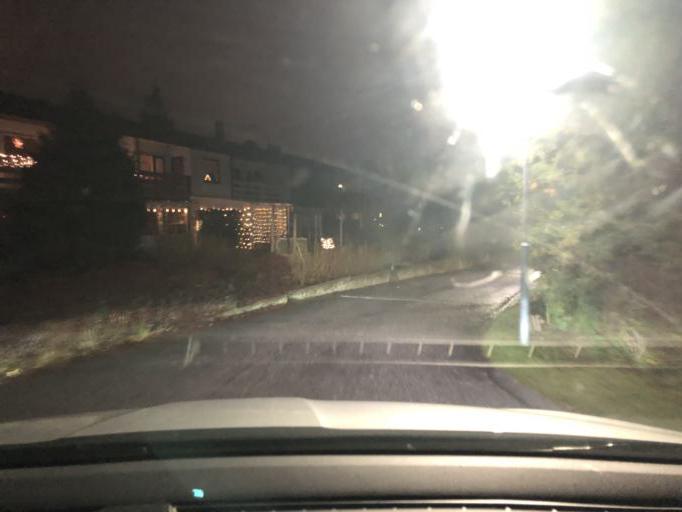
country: SE
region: Stockholm
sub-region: Jarfalla Kommun
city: Jakobsberg
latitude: 59.4041
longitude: 17.8064
